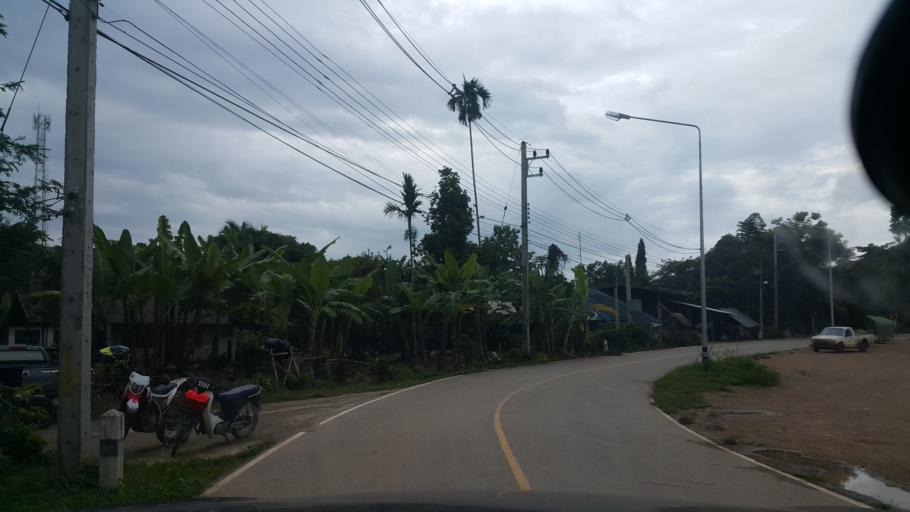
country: TH
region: Chiang Mai
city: San Sai
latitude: 18.9848
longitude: 99.1240
